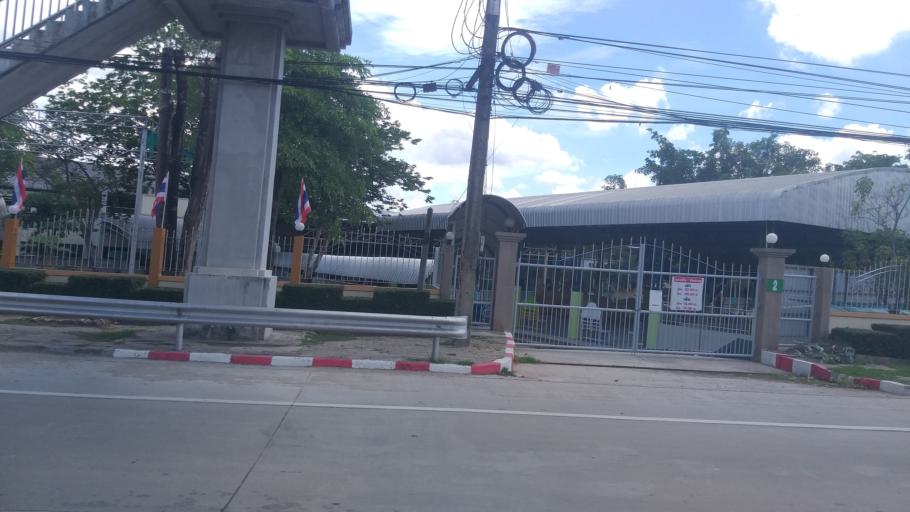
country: TH
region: Nakhon Nayok
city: Ban Na
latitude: 14.2639
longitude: 101.0654
